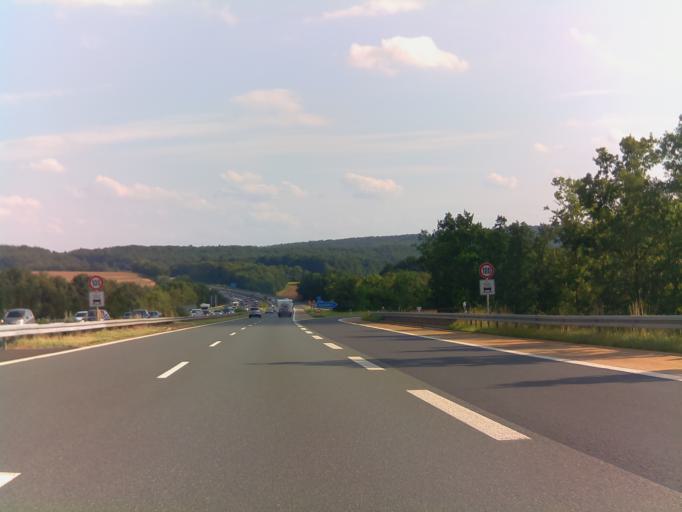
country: DE
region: Bavaria
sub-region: Regierungsbezirk Unterfranken
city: Oberthulba
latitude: 50.1990
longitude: 9.9385
